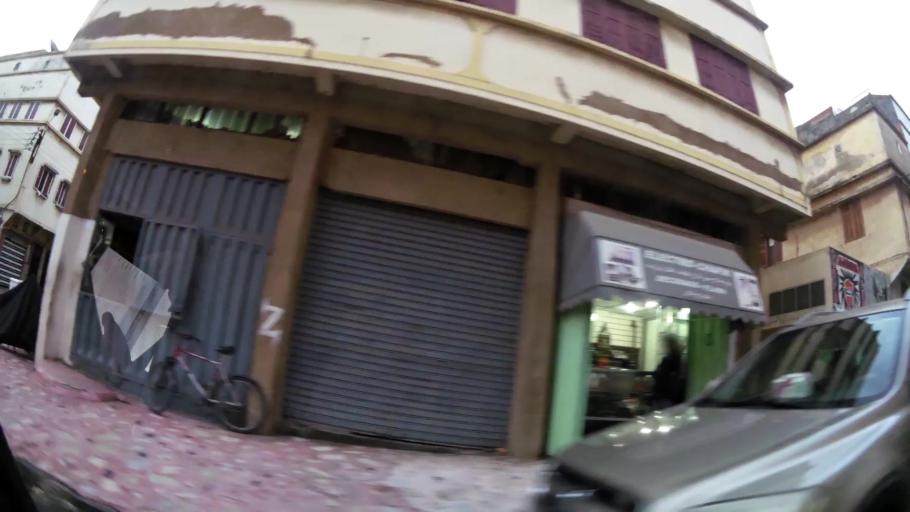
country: MA
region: Grand Casablanca
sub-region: Casablanca
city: Casablanca
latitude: 33.5537
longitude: -7.5856
